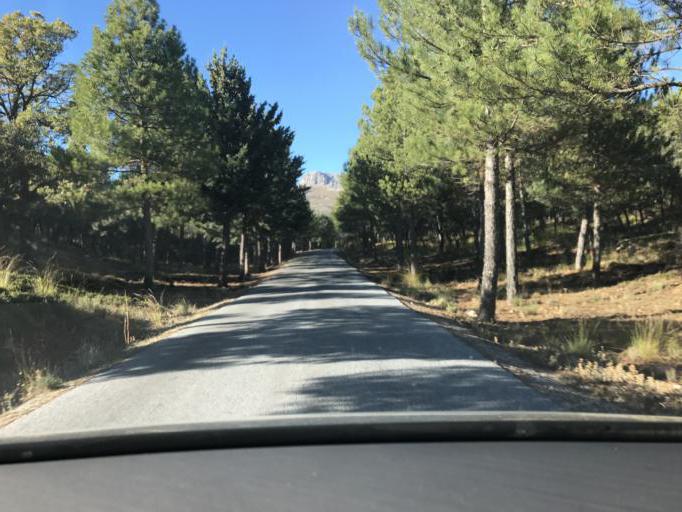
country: ES
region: Andalusia
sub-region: Provincia de Granada
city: Beas de Granada
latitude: 37.3027
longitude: -3.4433
